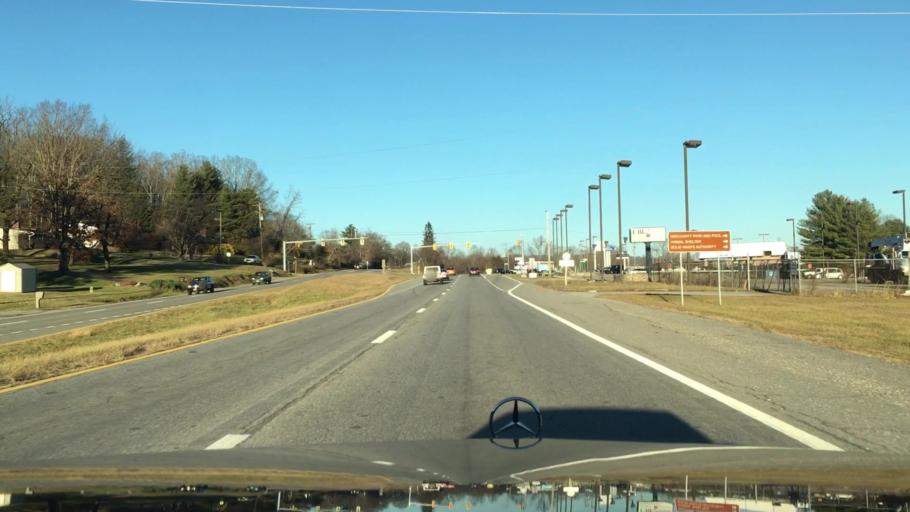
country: US
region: Virginia
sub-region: Montgomery County
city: Merrimac
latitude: 37.1787
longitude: -80.4146
